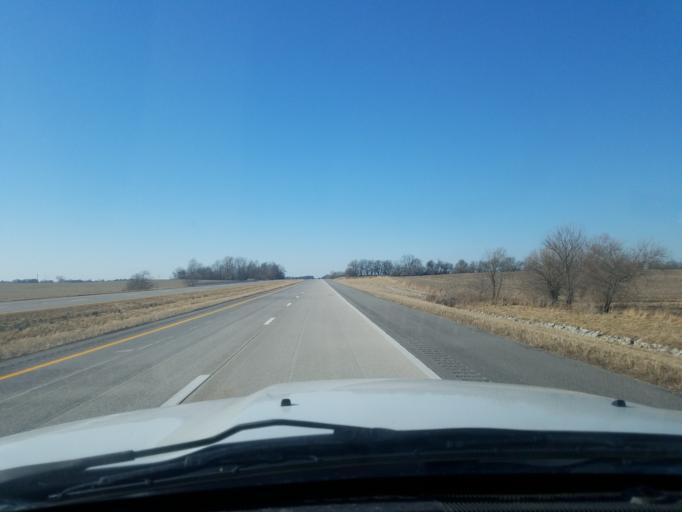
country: US
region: Kentucky
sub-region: Henderson County
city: Henderson
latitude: 37.7951
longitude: -87.4980
